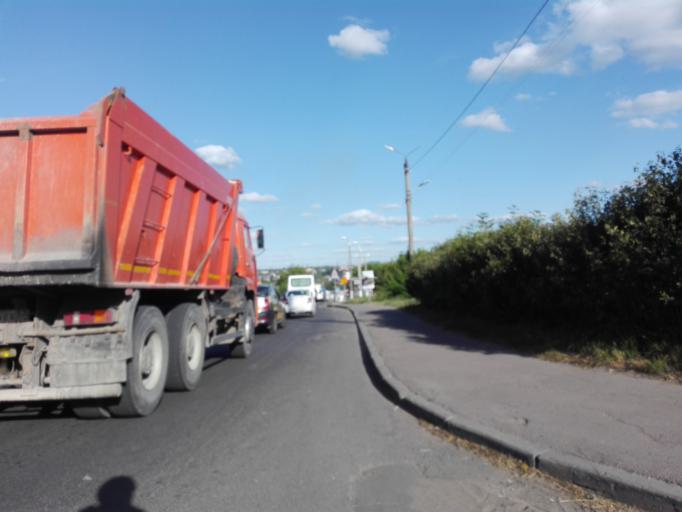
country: RU
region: Orjol
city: Orel
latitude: 52.9384
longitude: 36.0530
